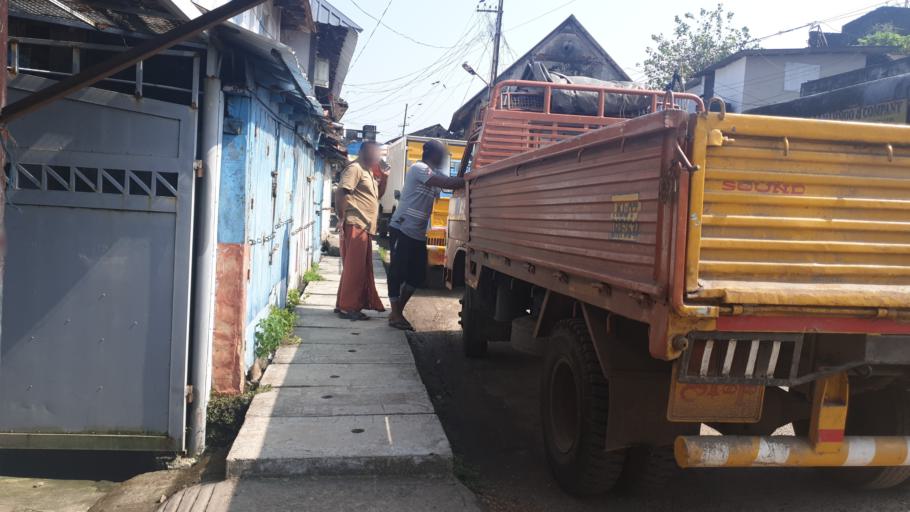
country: IN
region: Kerala
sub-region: Ernakulam
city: Cochin
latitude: 9.9659
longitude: 76.2540
